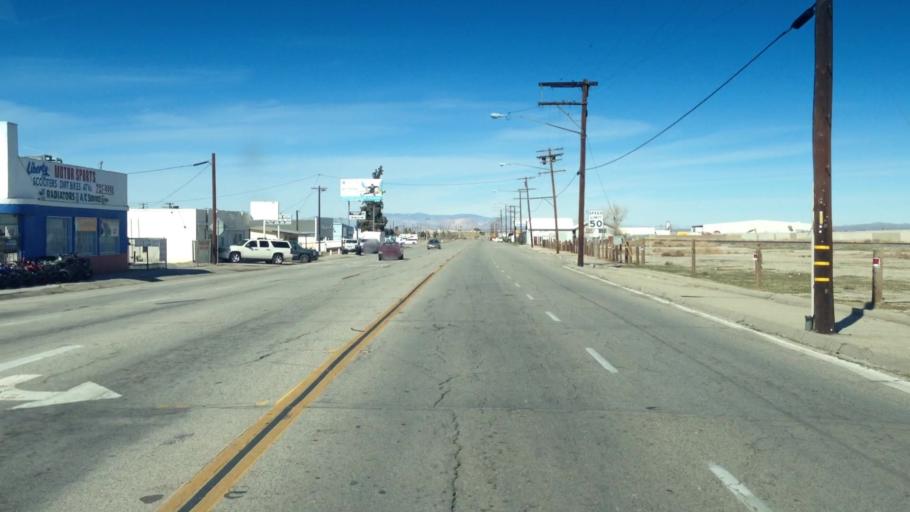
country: US
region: California
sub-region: Los Angeles County
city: Lancaster
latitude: 34.7042
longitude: -118.1379
